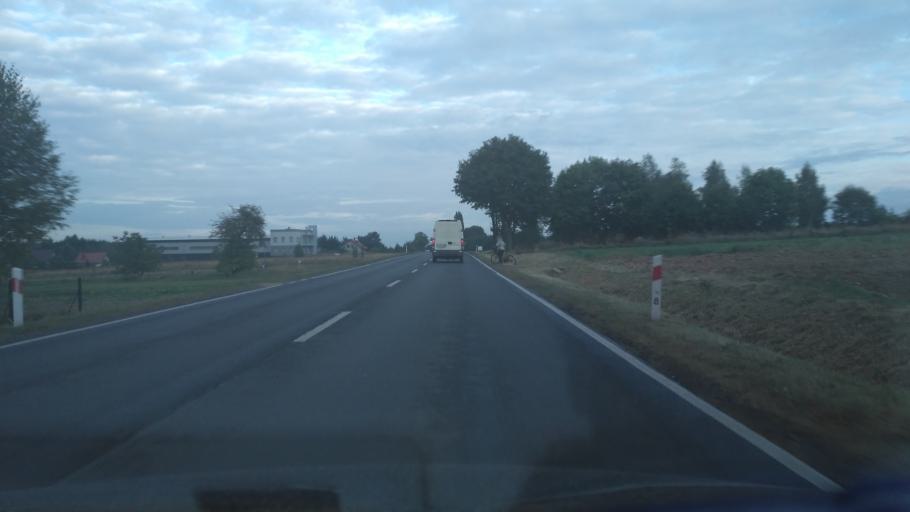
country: PL
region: Lublin Voivodeship
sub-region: Powiat leczynski
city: Spiczyn
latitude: 51.3031
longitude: 22.7399
